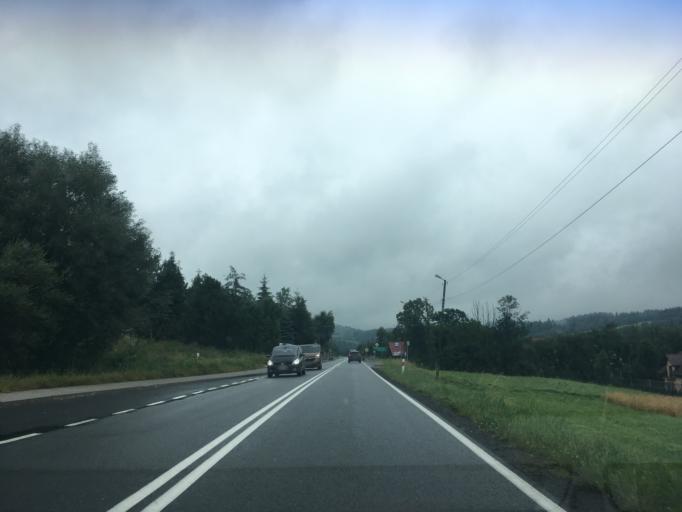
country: PL
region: Lesser Poland Voivodeship
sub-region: Powiat limanowski
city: Olszowka
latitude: 49.6365
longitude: 20.0211
